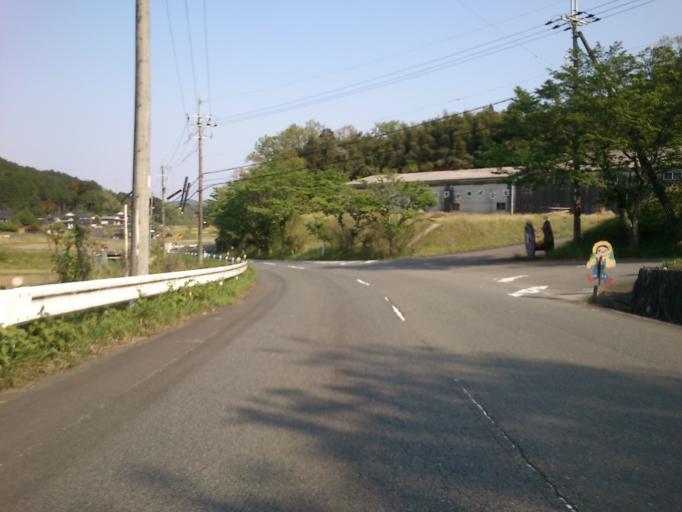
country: JP
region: Kyoto
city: Fukuchiyama
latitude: 35.2991
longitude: 135.0764
